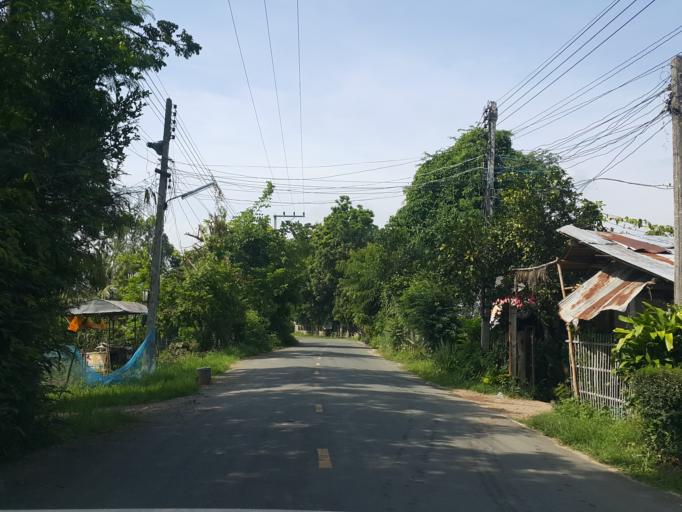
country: TH
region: Chiang Mai
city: San Kamphaeng
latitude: 18.7176
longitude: 99.0947
